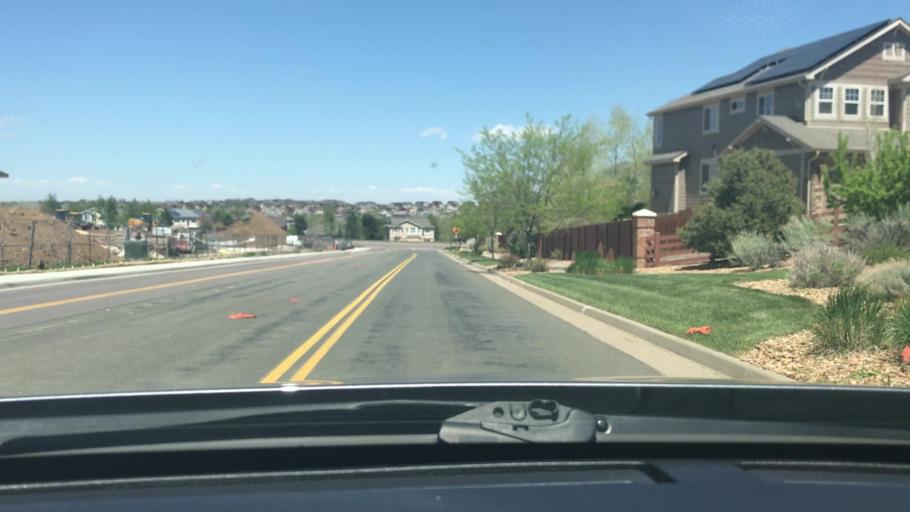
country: US
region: Colorado
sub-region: Arapahoe County
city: Dove Valley
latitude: 39.6513
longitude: -104.7438
